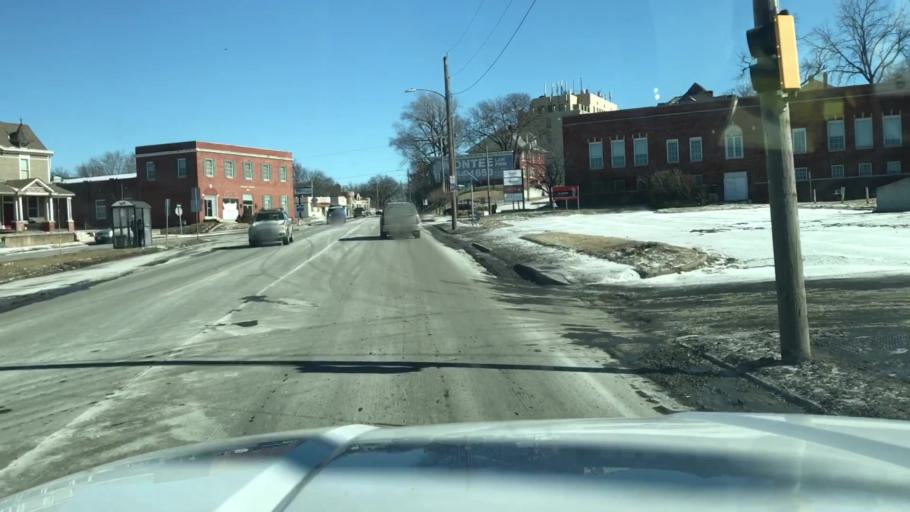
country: US
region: Missouri
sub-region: Buchanan County
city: Saint Joseph
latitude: 39.7755
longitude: -94.8337
